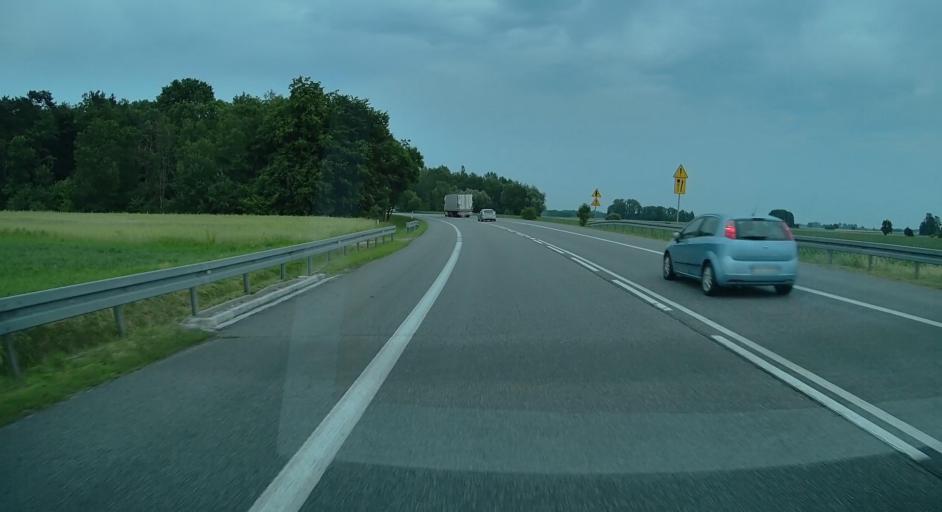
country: PL
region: Lublin Voivodeship
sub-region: Powiat lukowski
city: Trzebieszow
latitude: 52.0572
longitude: 22.5878
